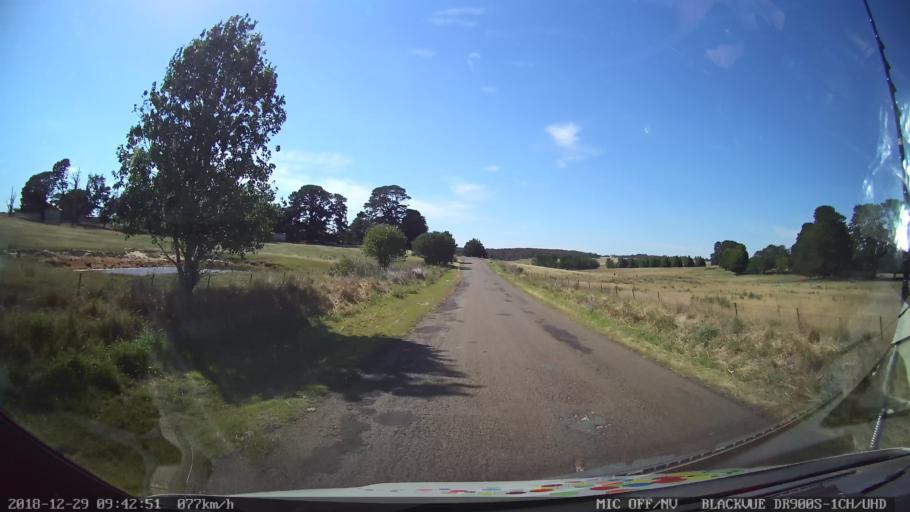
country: AU
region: New South Wales
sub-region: Upper Lachlan Shire
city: Crookwell
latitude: -34.6740
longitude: 149.4227
